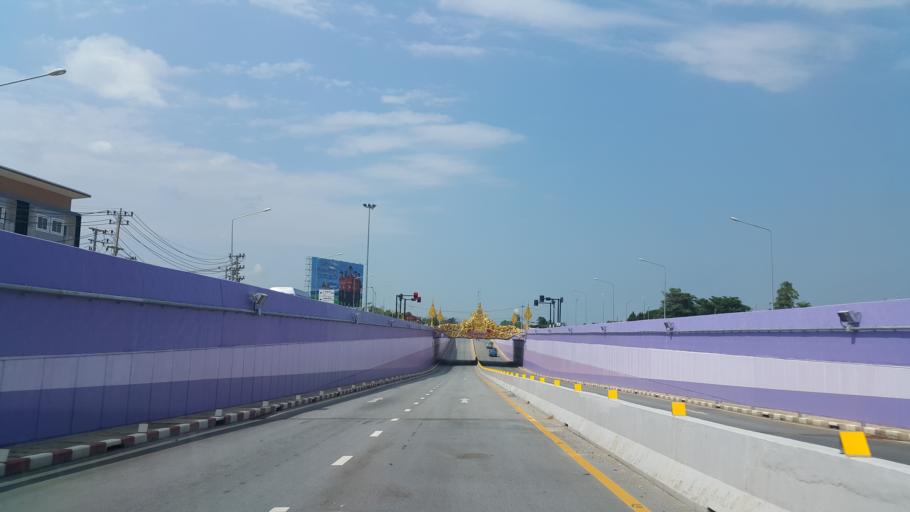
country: TH
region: Chiang Rai
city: Chiang Rai
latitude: 19.9632
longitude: 99.8819
